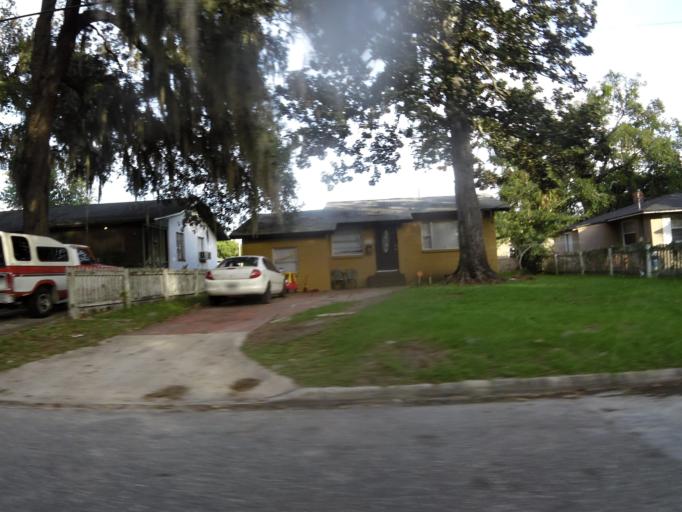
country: US
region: Florida
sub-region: Duval County
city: Jacksonville
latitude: 30.3866
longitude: -81.6496
